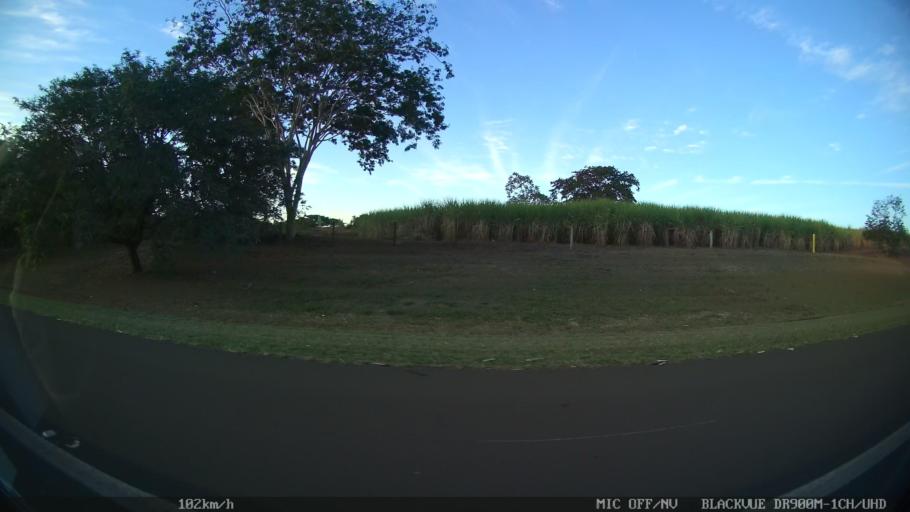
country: BR
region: Sao Paulo
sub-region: Pindorama
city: Pindorama
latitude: -21.2039
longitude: -48.9365
